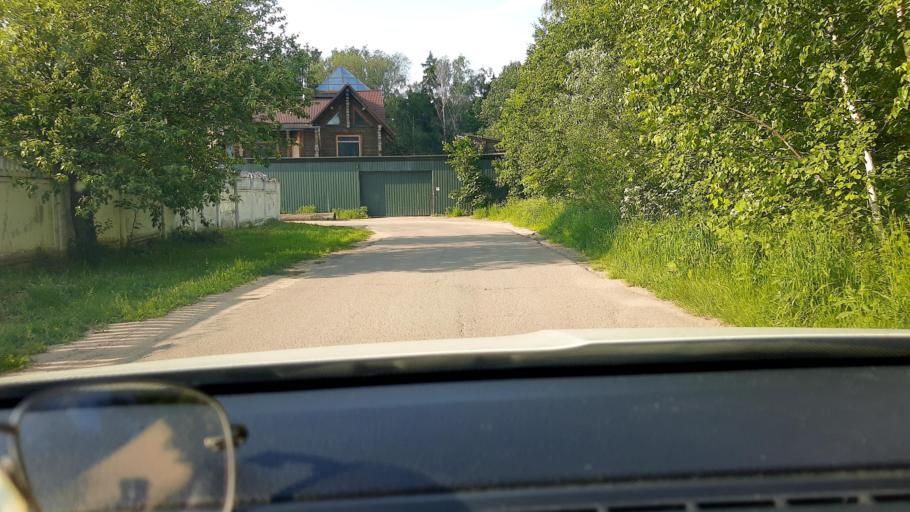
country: RU
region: Moscow
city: Novo-Peredelkino
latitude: 55.6698
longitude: 37.3216
